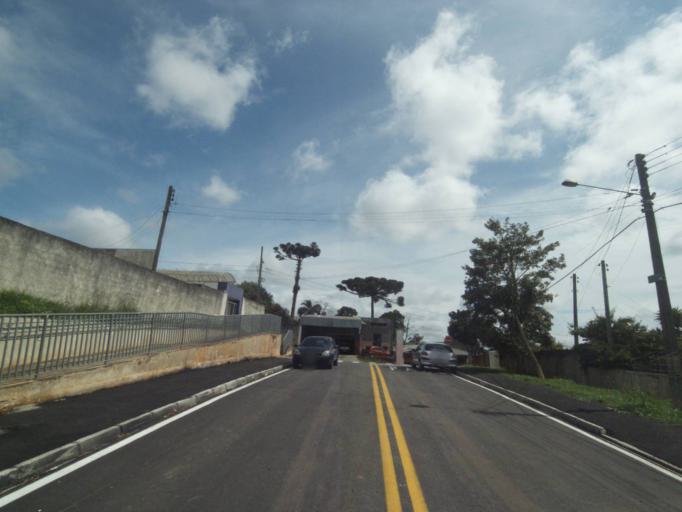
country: BR
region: Parana
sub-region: Quatro Barras
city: Quatro Barras
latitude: -25.3343
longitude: -49.0785
